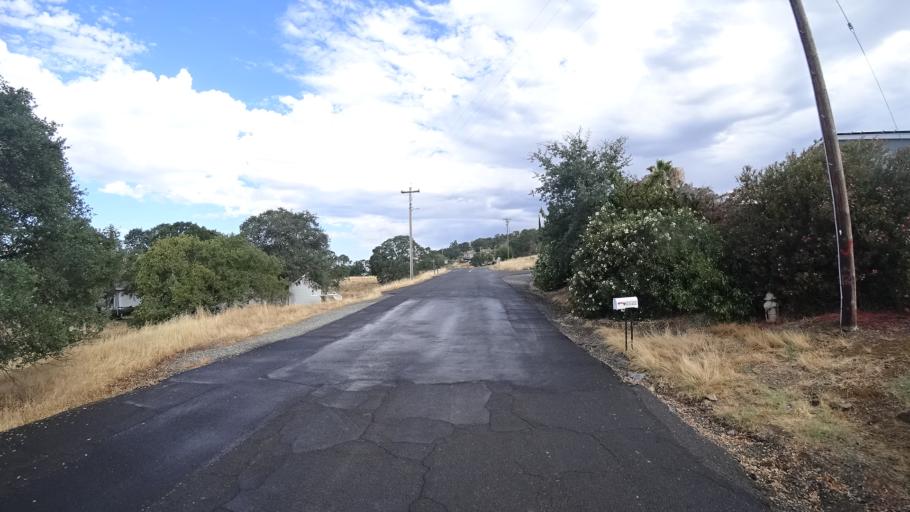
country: US
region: California
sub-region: Calaveras County
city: Copperopolis
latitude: 37.9080
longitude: -120.6136
